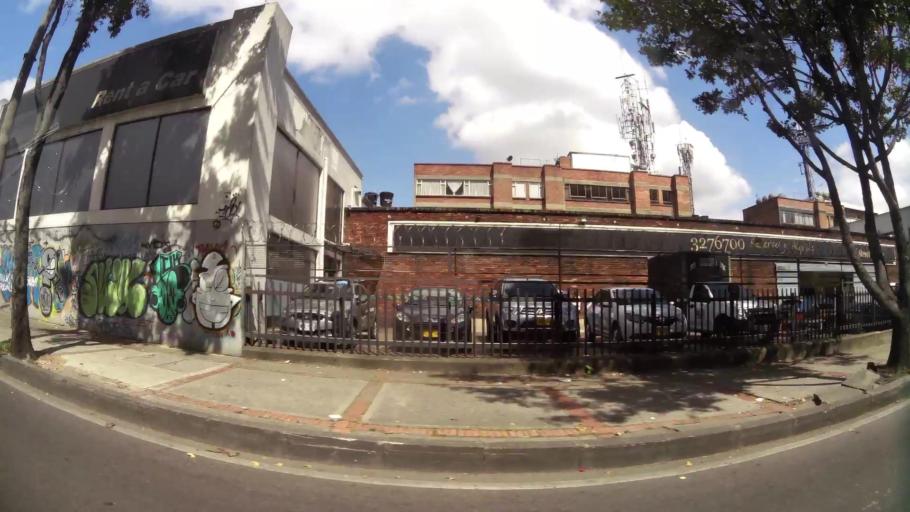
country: CO
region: Bogota D.C.
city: Bogota
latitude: 4.6165
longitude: -74.0724
